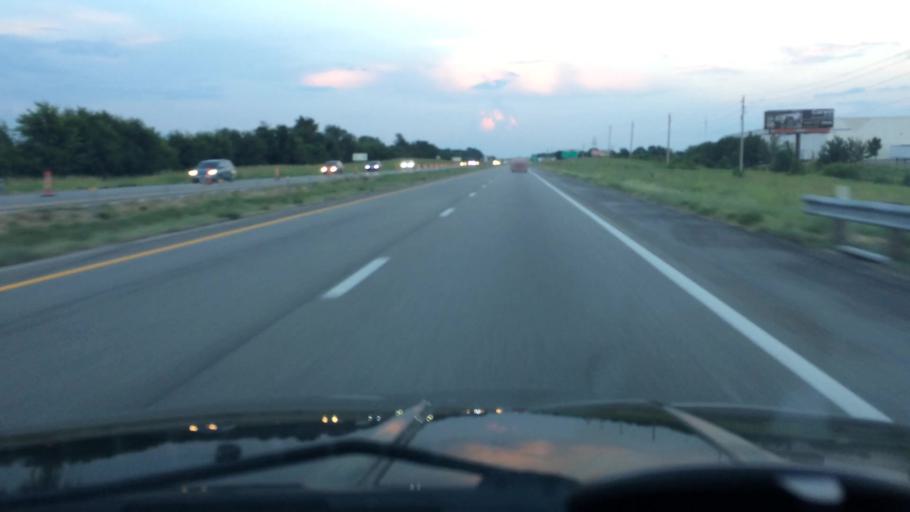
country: US
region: Missouri
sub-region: Greene County
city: Springfield
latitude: 37.2501
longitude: -93.2115
